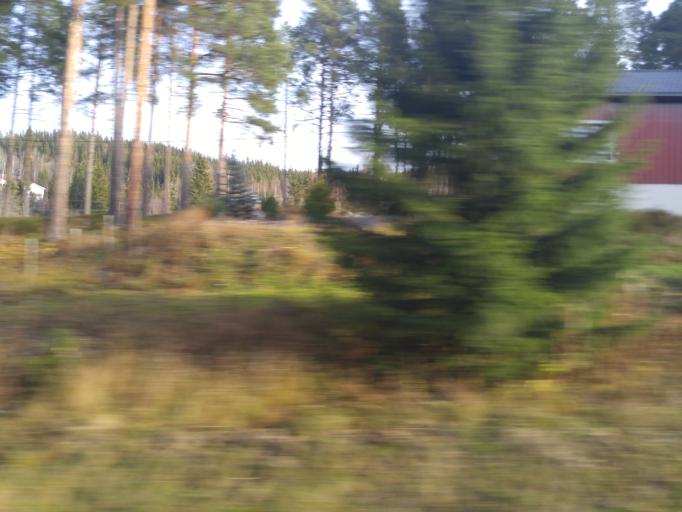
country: NO
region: Oppland
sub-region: Nord-Aurdal
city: Fagernes
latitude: 61.0590
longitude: 9.1644
